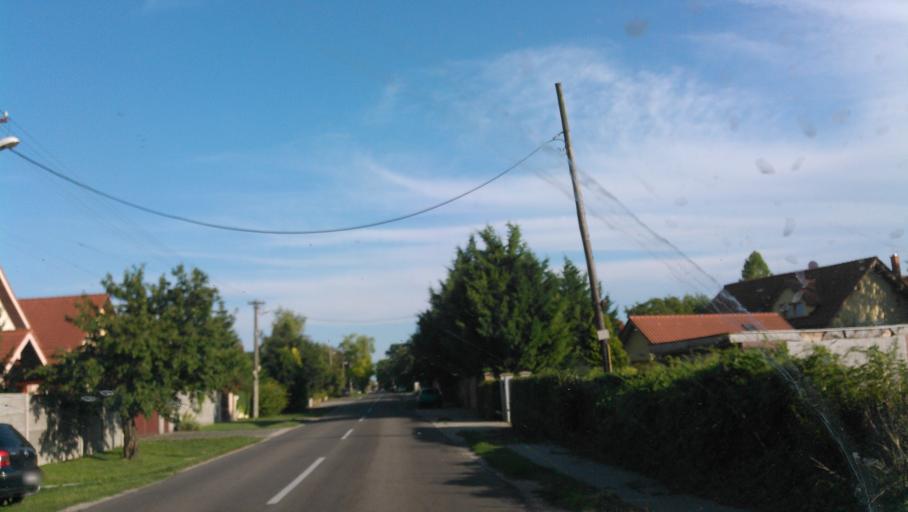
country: SK
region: Bratislavsky
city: Dunajska Luzna
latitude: 48.1733
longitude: 17.2730
